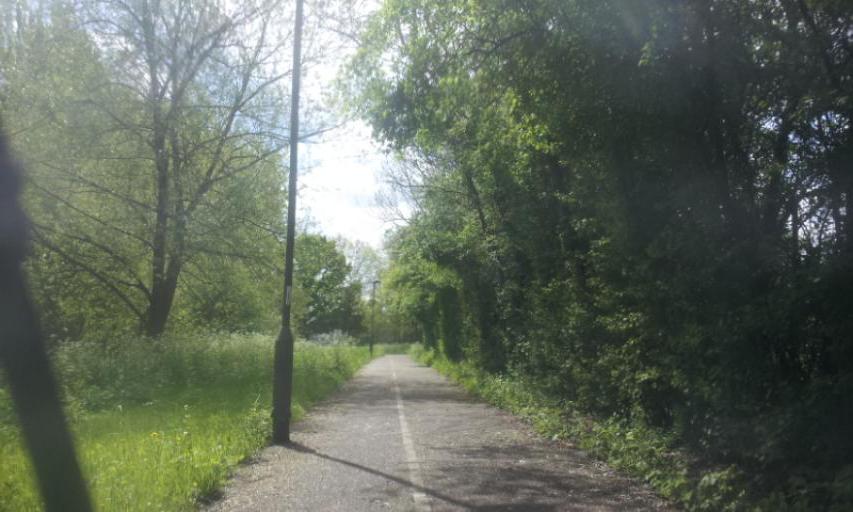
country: GB
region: England
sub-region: Greater London
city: Beckenham
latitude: 51.4192
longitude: -0.0396
